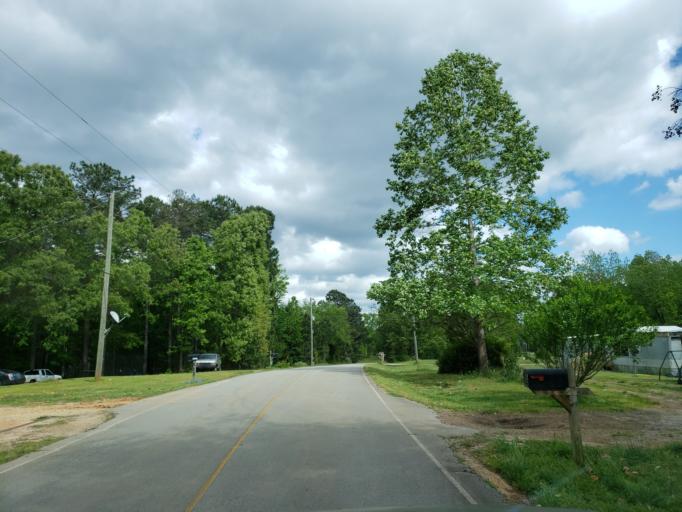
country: US
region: Georgia
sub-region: Haralson County
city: Tallapoosa
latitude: 33.6829
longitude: -85.3132
